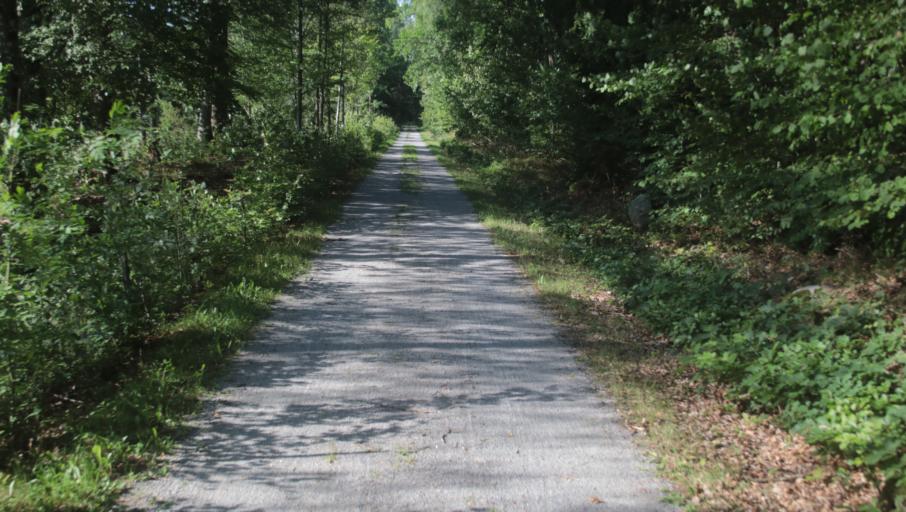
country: SE
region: Blekinge
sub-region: Karlshamns Kommun
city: Svangsta
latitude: 56.3696
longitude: 14.6841
